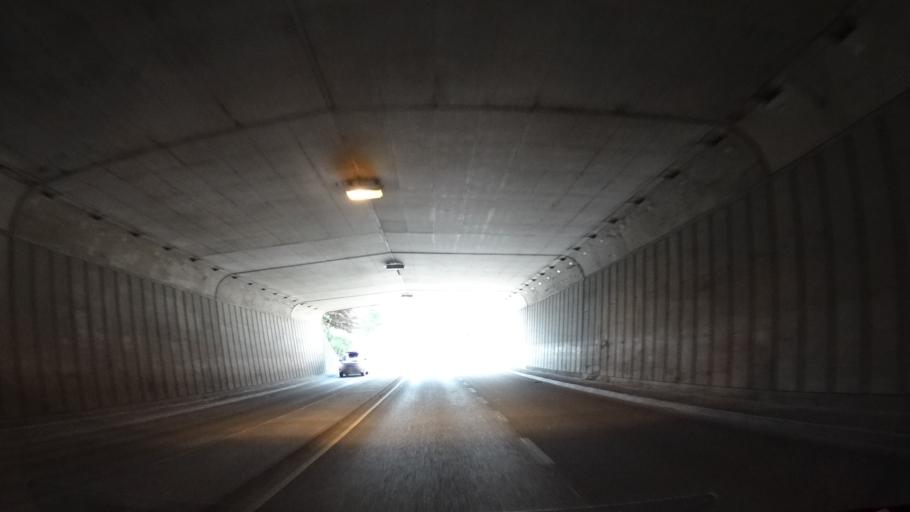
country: NO
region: Rogaland
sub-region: Stavanger
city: Stavanger
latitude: 58.9702
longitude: 5.7479
